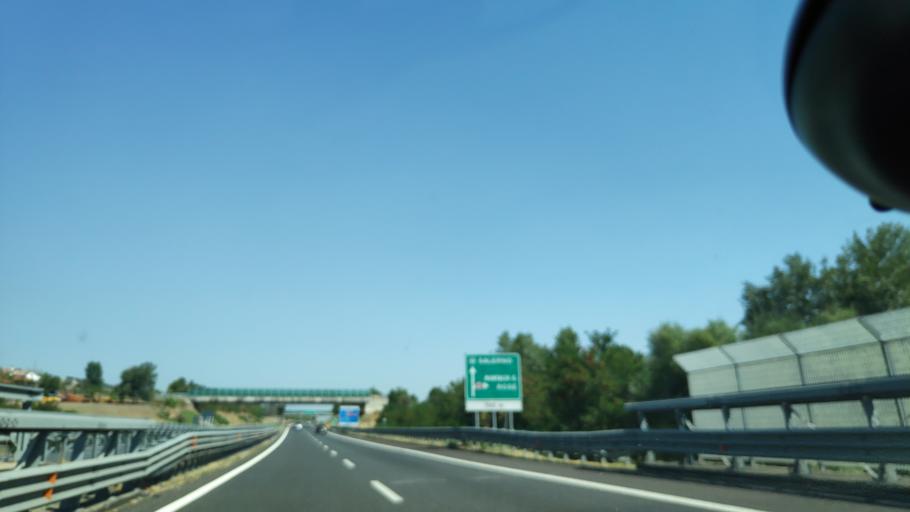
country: IT
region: Calabria
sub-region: Provincia di Cosenza
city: Stazione Montalto-Coretto
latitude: 39.4158
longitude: 16.2443
